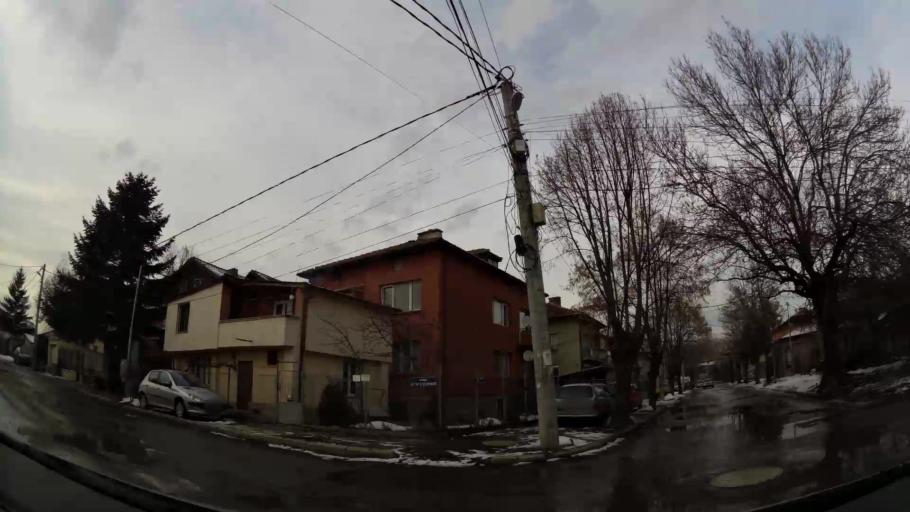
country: BG
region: Sofia-Capital
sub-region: Stolichna Obshtina
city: Sofia
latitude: 42.7241
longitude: 23.3350
